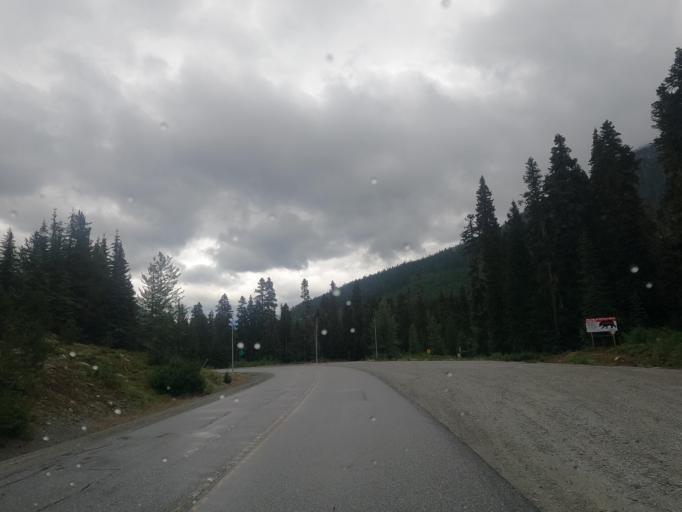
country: CA
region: British Columbia
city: Pemberton
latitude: 50.3801
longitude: -122.4754
